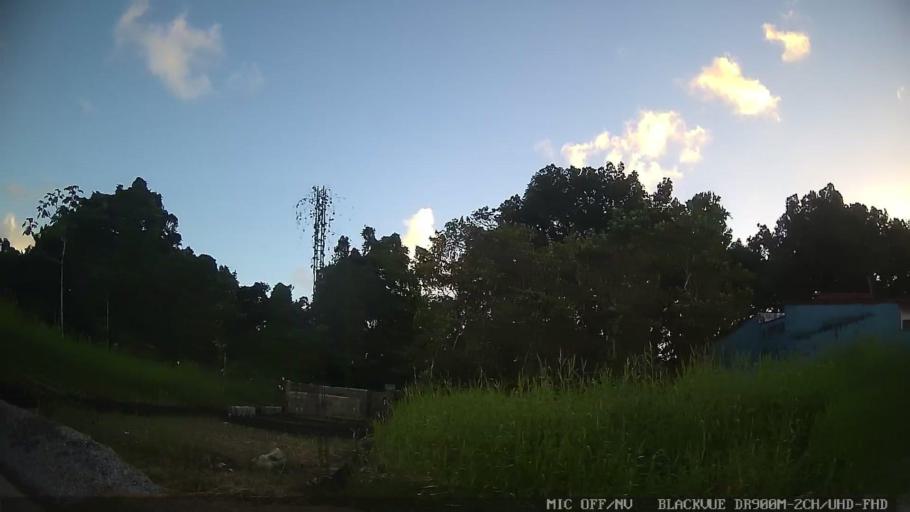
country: BR
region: Sao Paulo
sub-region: Itanhaem
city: Itanhaem
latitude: -24.1425
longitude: -46.7331
